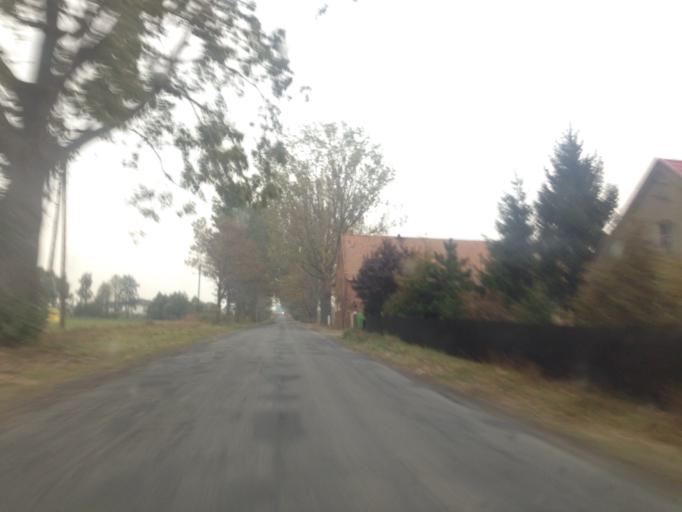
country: PL
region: Greater Poland Voivodeship
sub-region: Powiat poznanski
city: Kleszczewo
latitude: 52.3493
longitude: 17.1504
